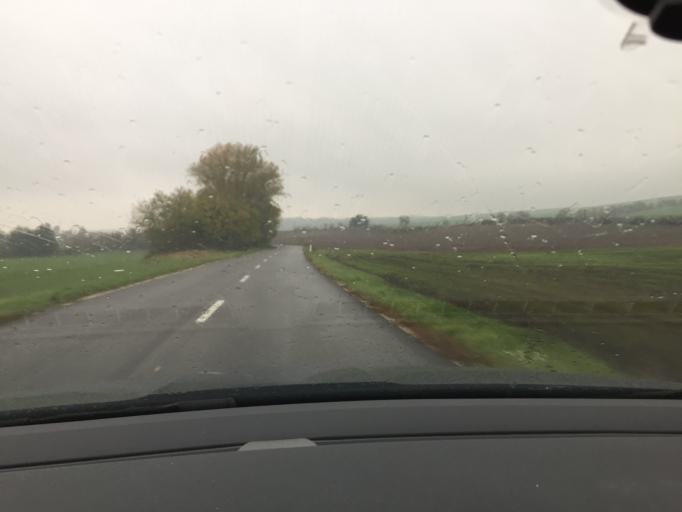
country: SK
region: Nitriansky
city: Zeliezovce
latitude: 47.9843
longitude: 18.7620
